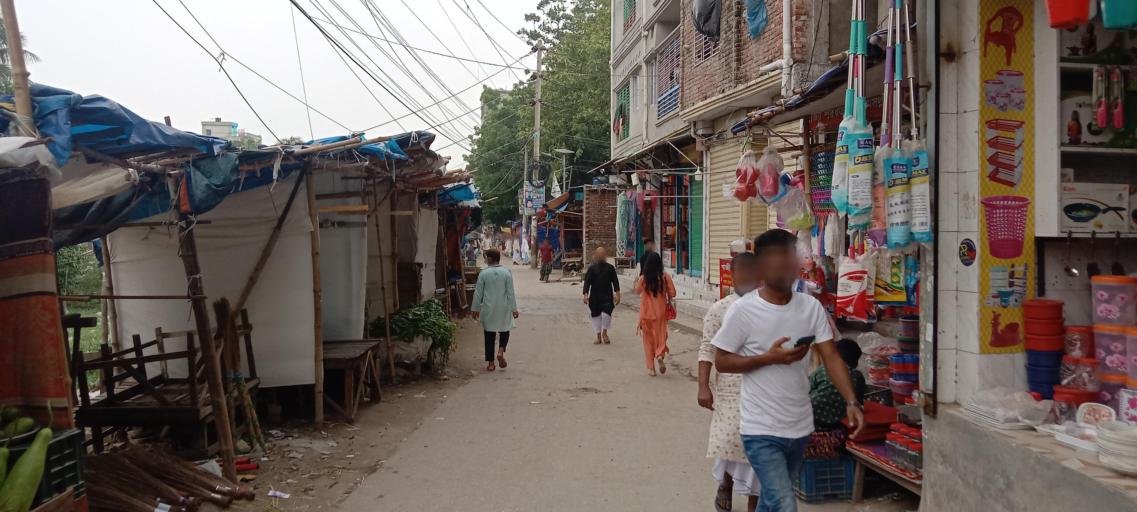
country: BD
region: Dhaka
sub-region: Dhaka
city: Dhaka
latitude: 23.6998
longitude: 90.4076
